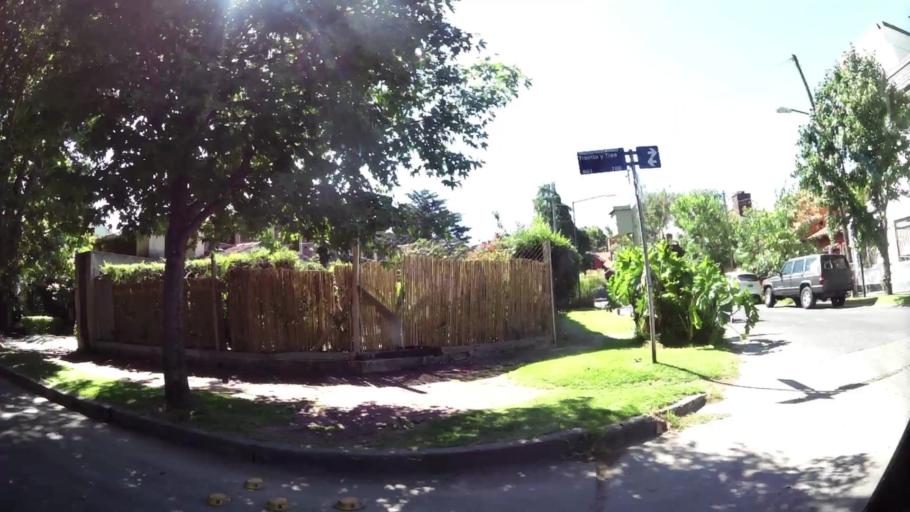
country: AR
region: Buenos Aires
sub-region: Partido de San Isidro
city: San Isidro
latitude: -34.4549
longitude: -58.5264
